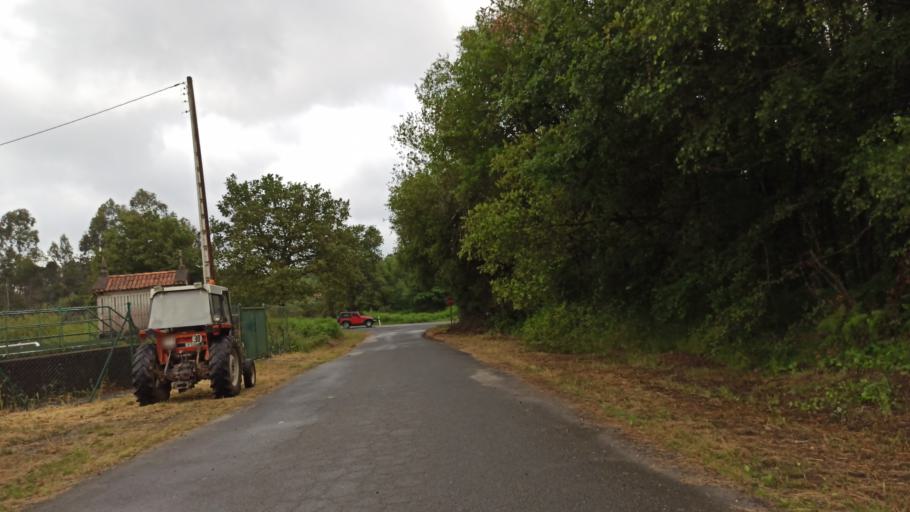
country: ES
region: Galicia
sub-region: Provincia da Coruna
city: Santiso
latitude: 42.7626
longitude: -8.0272
